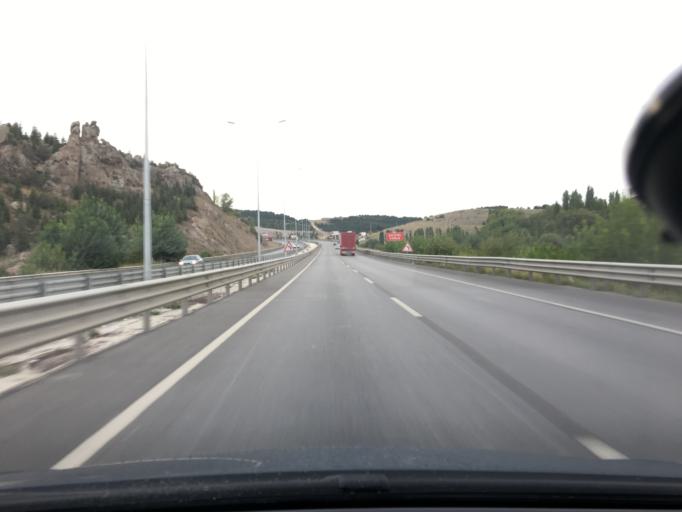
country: TR
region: Afyonkarahisar
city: Afyonkarahisar
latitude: 38.7936
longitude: 30.4459
